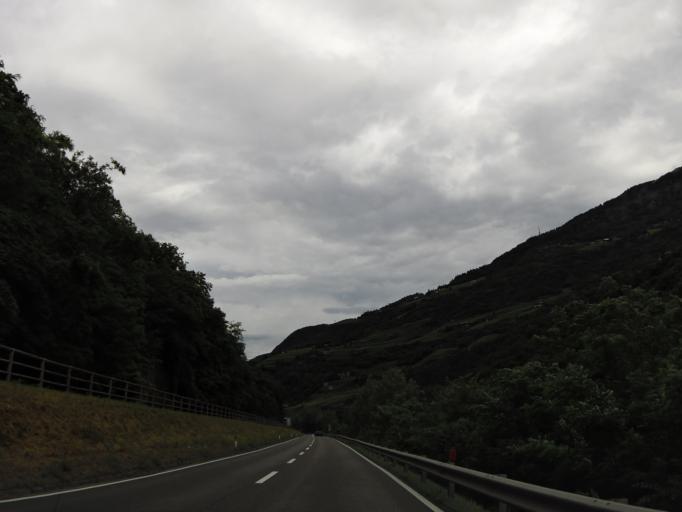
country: IT
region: Trentino-Alto Adige
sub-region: Bolzano
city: Cornedo All'Isarco
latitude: 46.4913
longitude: 11.4164
